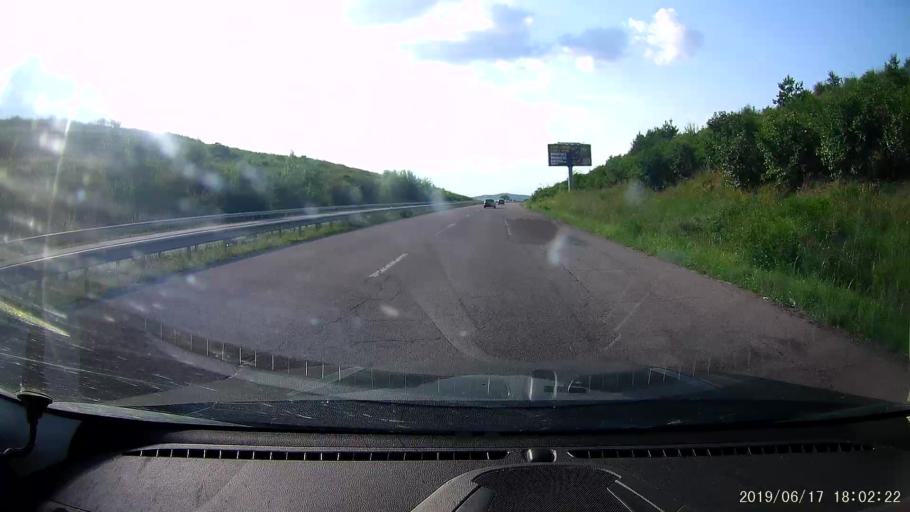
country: BG
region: Khaskovo
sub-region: Obshtina Svilengrad
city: Svilengrad
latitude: 41.7585
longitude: 26.2320
